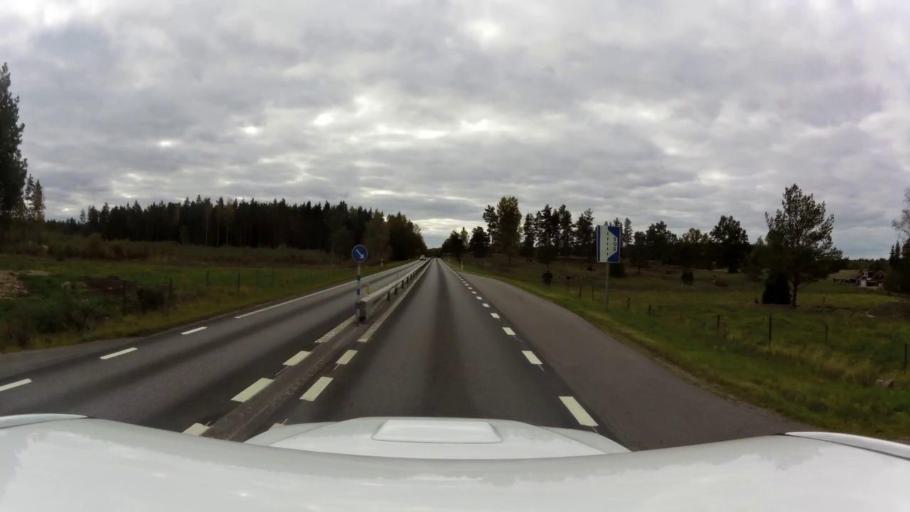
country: SE
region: OEstergoetland
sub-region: Linkopings Kommun
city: Malmslatt
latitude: 58.3005
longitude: 15.5639
